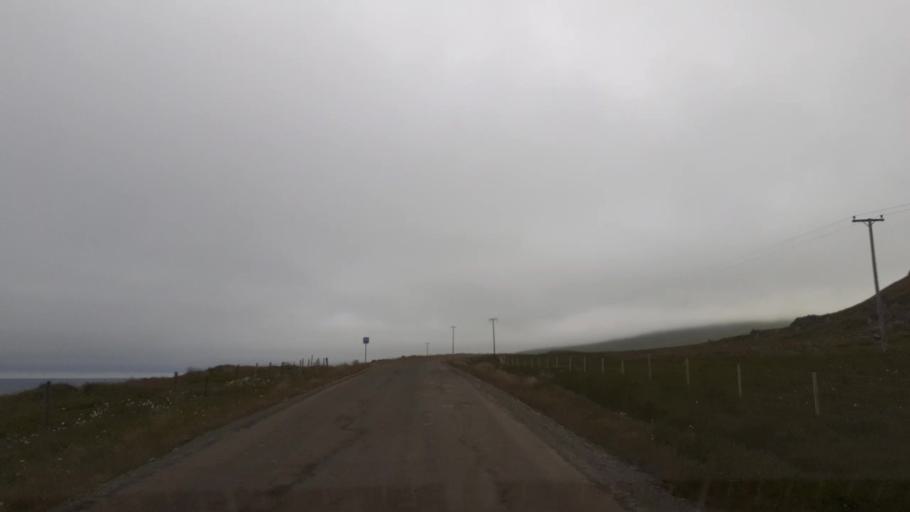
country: IS
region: Northwest
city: Saudarkrokur
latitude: 65.5206
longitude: -20.9667
